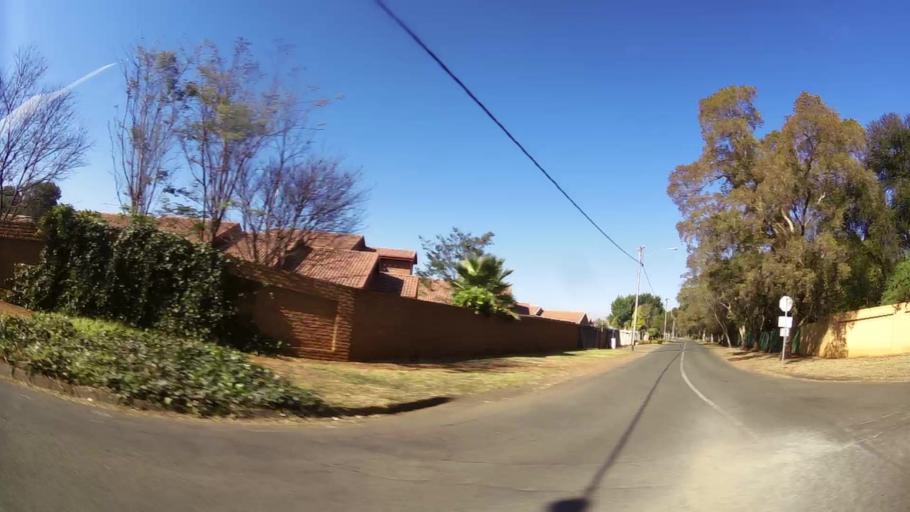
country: ZA
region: Gauteng
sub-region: City of Tshwane Metropolitan Municipality
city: Centurion
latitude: -25.8446
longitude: 28.2126
